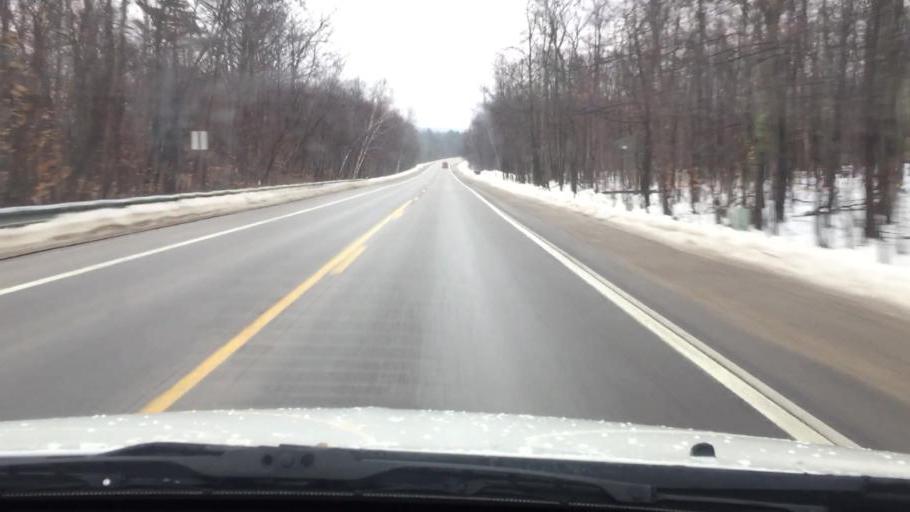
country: US
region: Michigan
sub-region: Charlevoix County
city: Charlevoix
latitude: 45.2637
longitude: -85.1976
